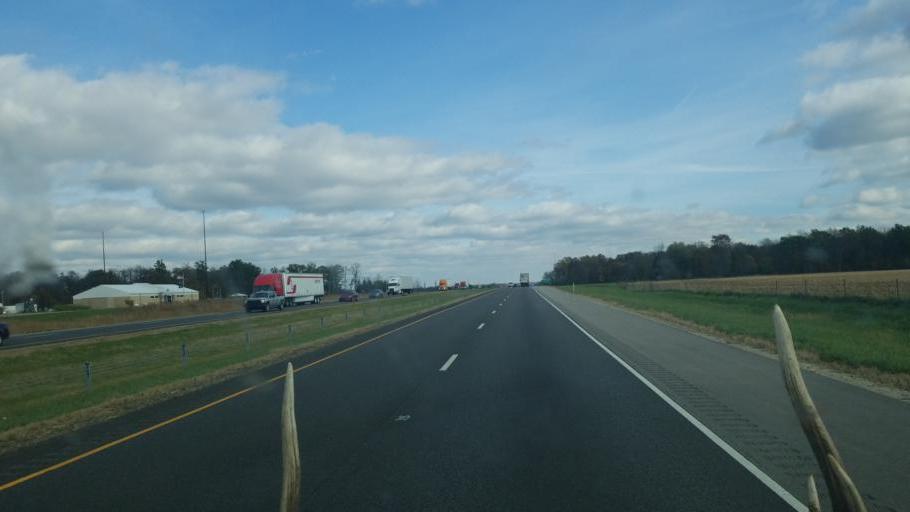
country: US
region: Indiana
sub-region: Wayne County
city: Centerville
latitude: 39.8594
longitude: -85.0287
